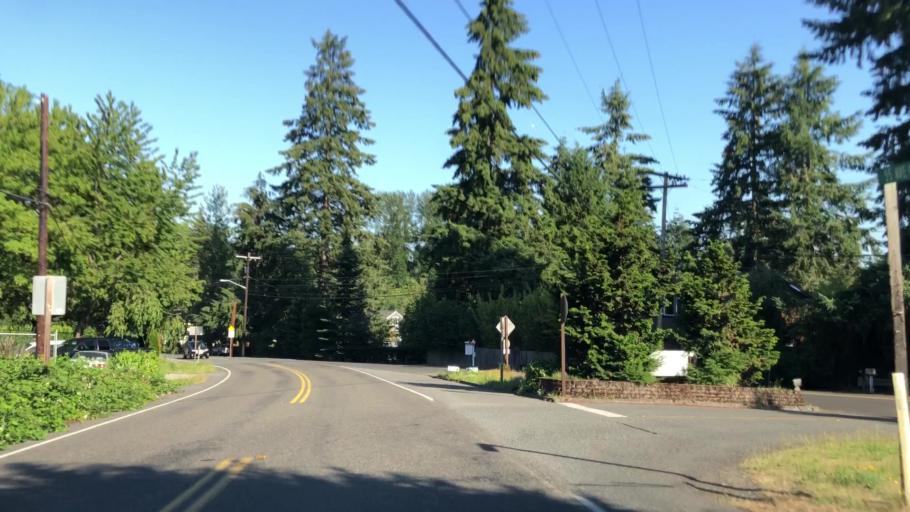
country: US
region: Washington
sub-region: Snohomish County
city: Brier
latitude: 47.7688
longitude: -122.2687
